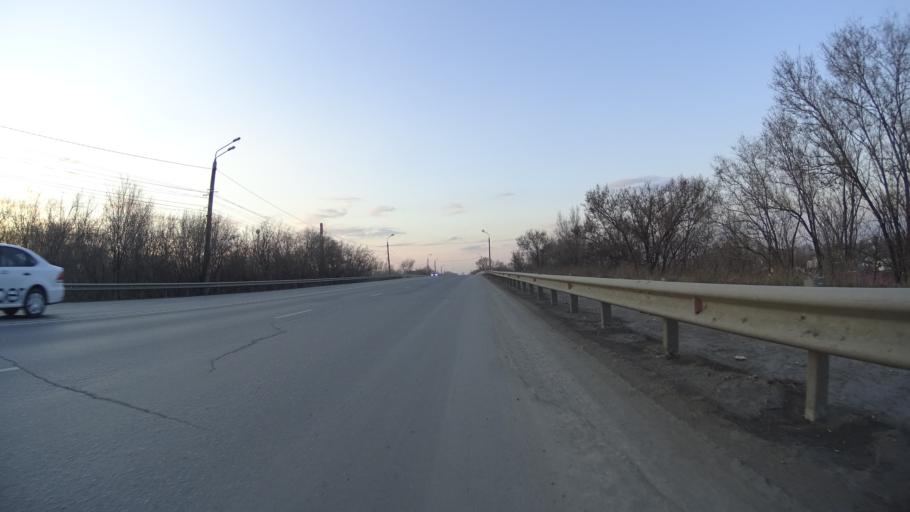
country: RU
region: Chelyabinsk
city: Novosineglazovskiy
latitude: 55.1009
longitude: 61.3877
